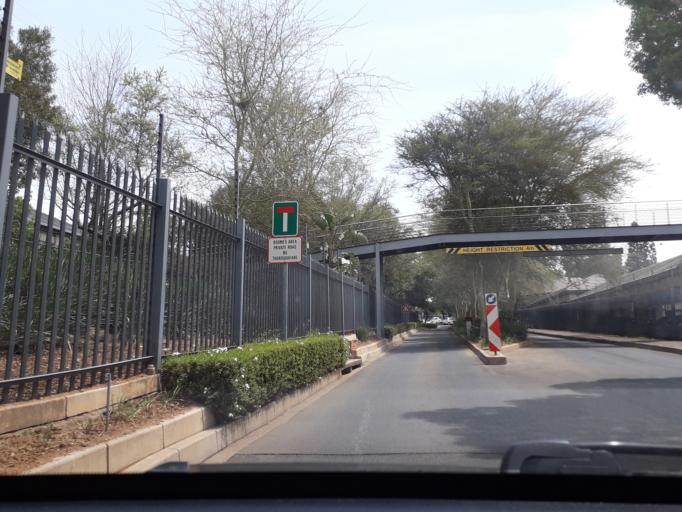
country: ZA
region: Gauteng
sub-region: City of Johannesburg Metropolitan Municipality
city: Diepsloot
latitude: -26.0441
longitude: 28.0202
